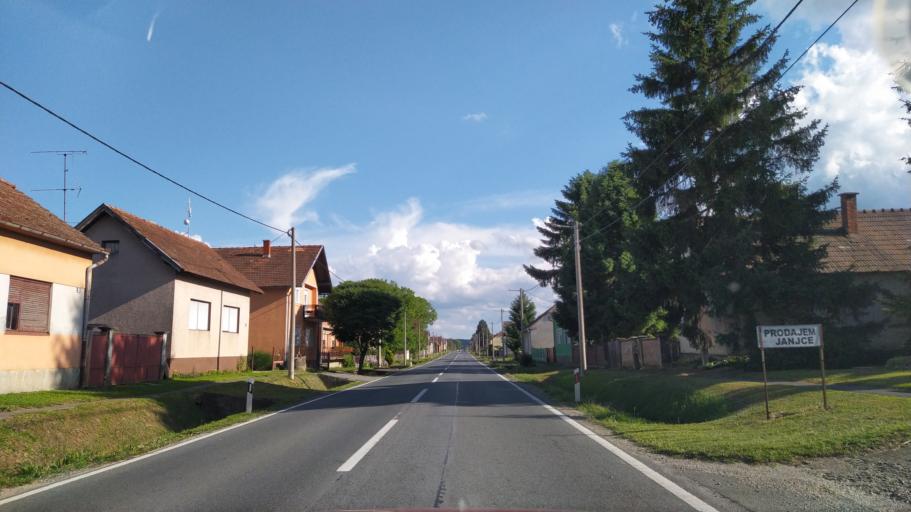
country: HR
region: Virovitick-Podravska
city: Spisic-Bukovica
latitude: 45.8870
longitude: 17.2893
